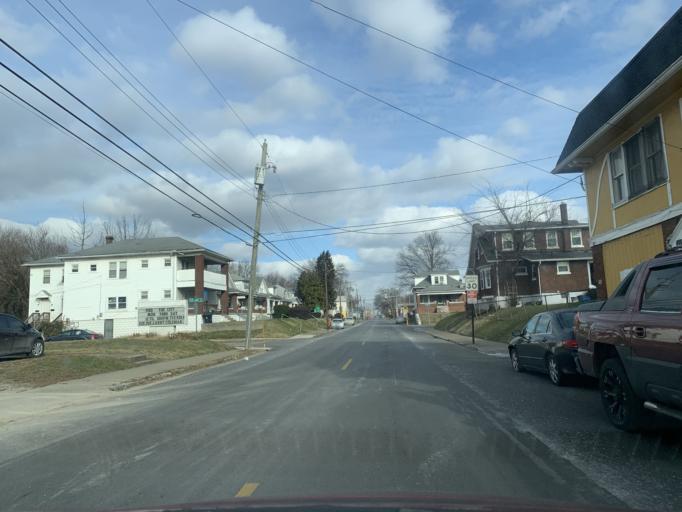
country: US
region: Kentucky
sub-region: Jefferson County
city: Louisville
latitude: 38.2401
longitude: -85.7959
